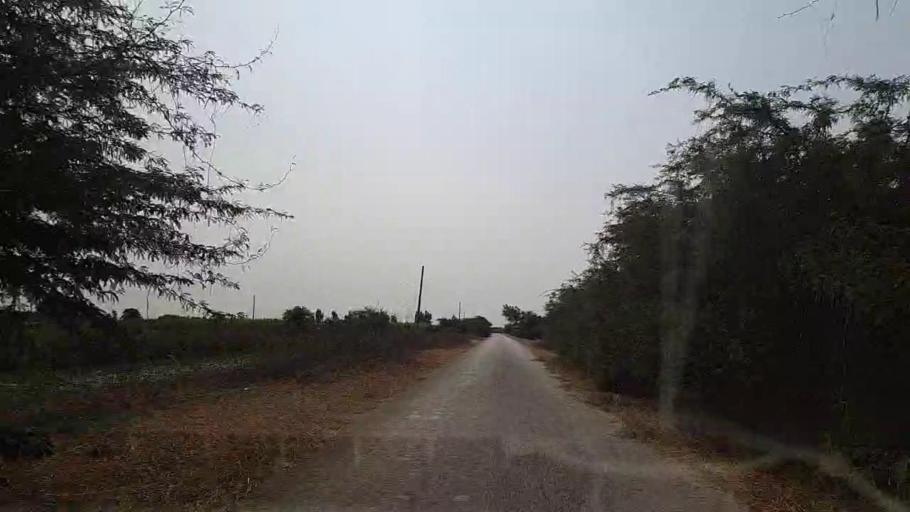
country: PK
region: Sindh
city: Chuhar Jamali
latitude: 24.3133
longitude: 67.9394
